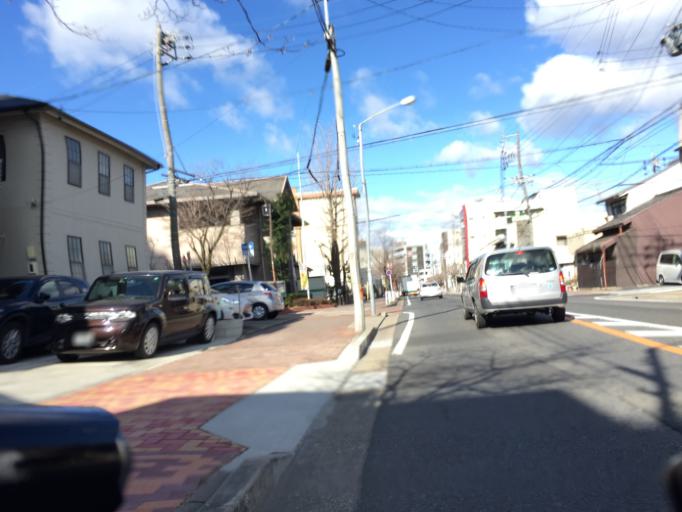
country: JP
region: Aichi
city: Nagoya-shi
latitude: 35.1627
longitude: 136.9354
